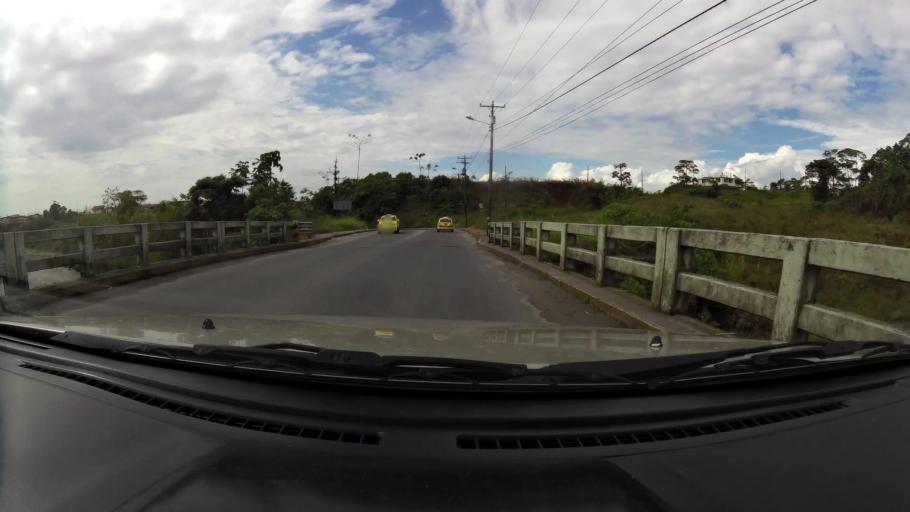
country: EC
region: Pastaza
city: Puyo
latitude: -1.4982
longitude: -78.0015
